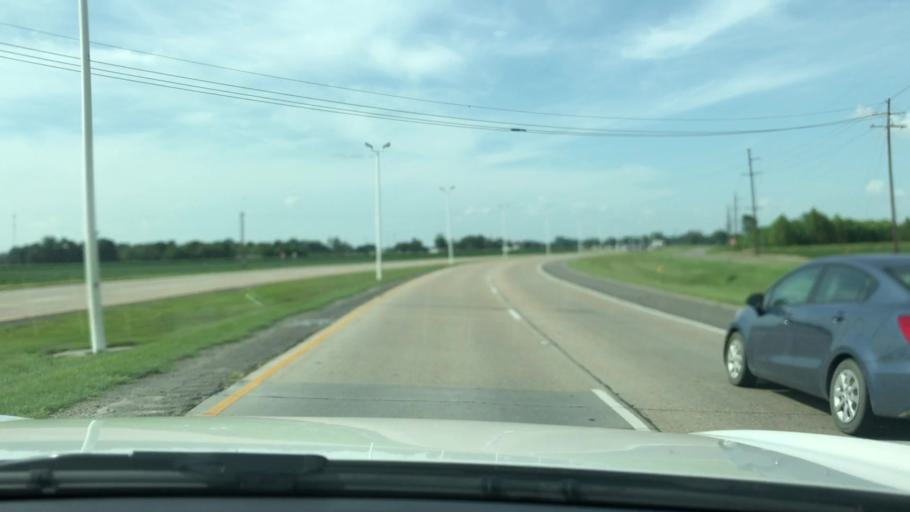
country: US
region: Louisiana
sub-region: West Baton Rouge Parish
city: Addis
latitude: 30.3426
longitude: -91.2609
